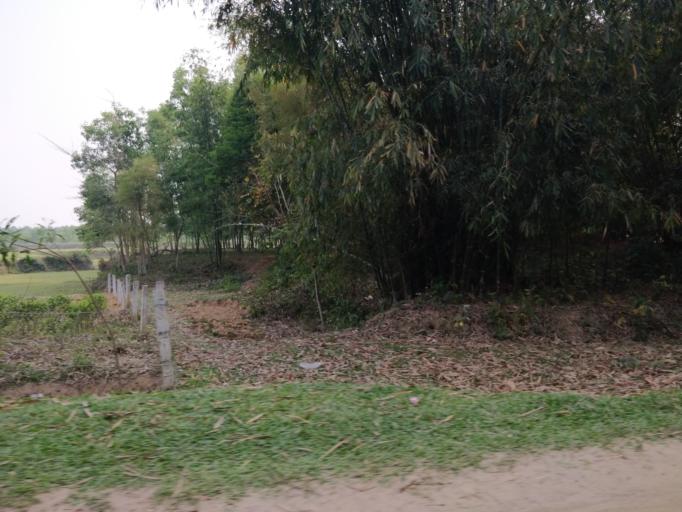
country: IN
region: Tripura
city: Khowai
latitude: 24.1295
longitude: 91.3776
